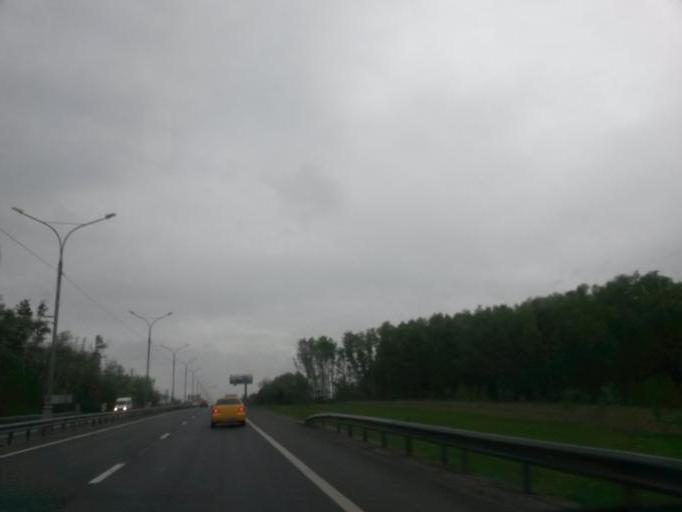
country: RU
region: Moskovskaya
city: Gorki-Leninskiye
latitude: 55.5163
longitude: 37.8268
